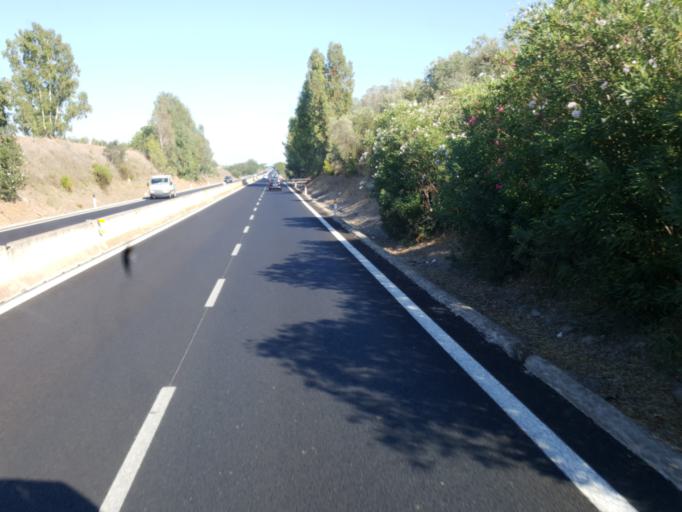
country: IT
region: Latium
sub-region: Provincia di Viterbo
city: Pescia Romana
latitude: 42.3993
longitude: 11.5102
